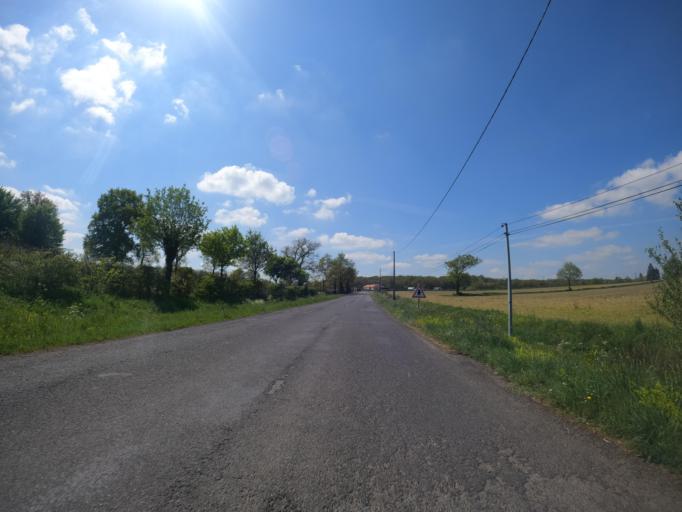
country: FR
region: Poitou-Charentes
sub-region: Departement des Deux-Sevres
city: Boisme
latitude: 46.7112
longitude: -0.4164
